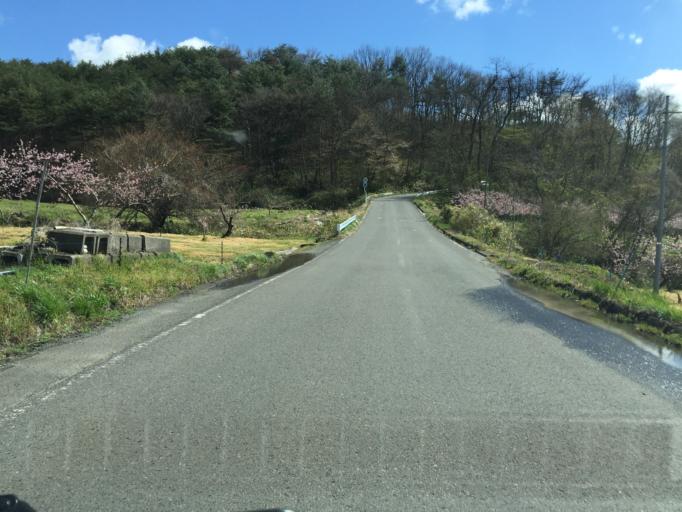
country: JP
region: Fukushima
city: Fukushima-shi
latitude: 37.8300
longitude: 140.4213
